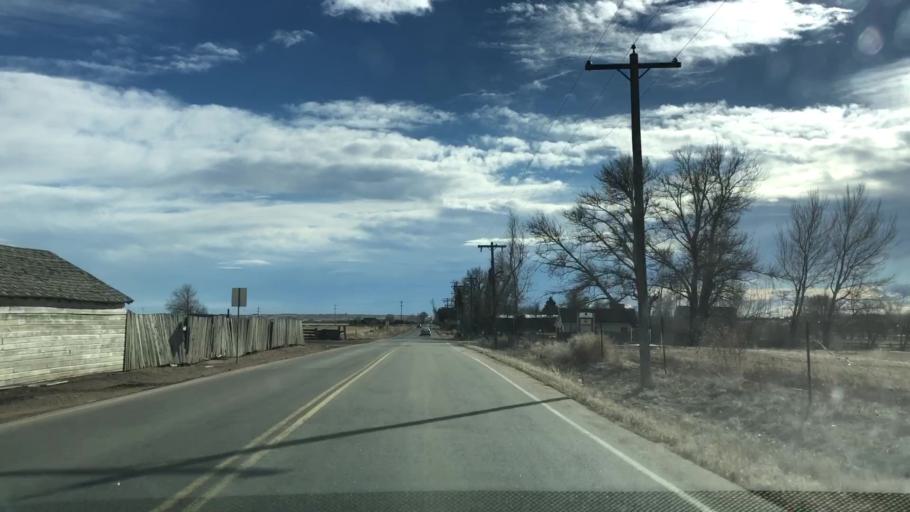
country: US
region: Colorado
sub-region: Weld County
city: Windsor
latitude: 40.5090
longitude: -104.9442
